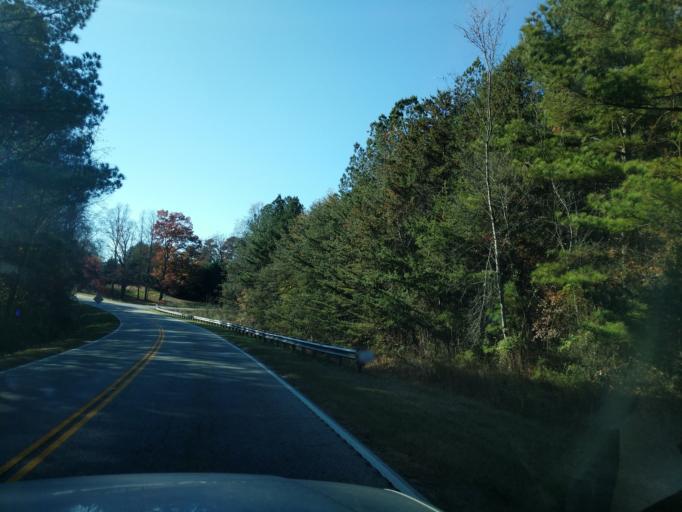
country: US
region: South Carolina
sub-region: Spartanburg County
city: Landrum
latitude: 35.1273
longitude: -82.1339
